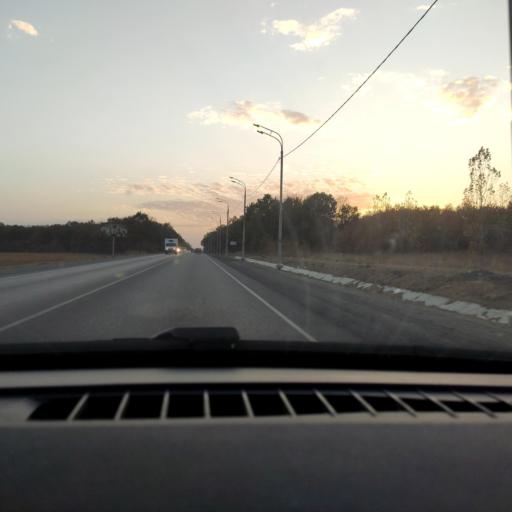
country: RU
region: Voronezj
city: Semiluki
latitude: 51.6434
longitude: 39.0183
